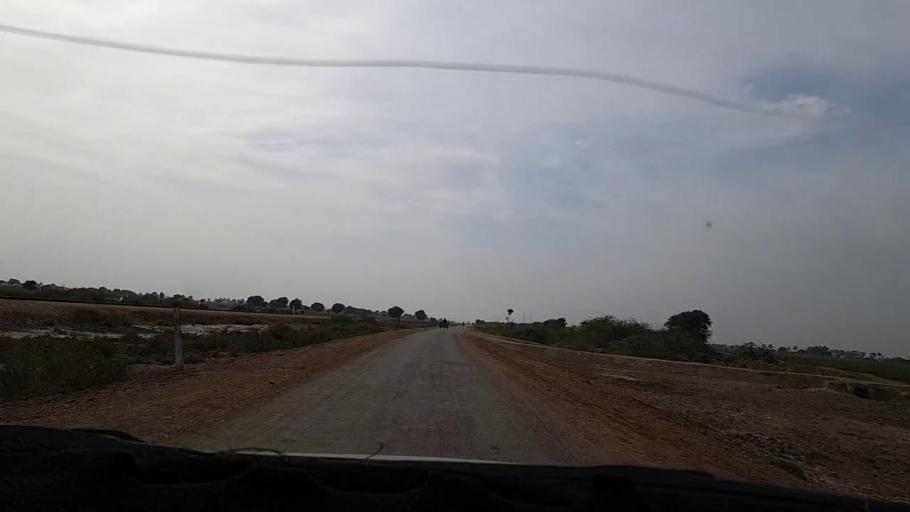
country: PK
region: Sindh
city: Pithoro
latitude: 25.5171
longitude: 69.2592
